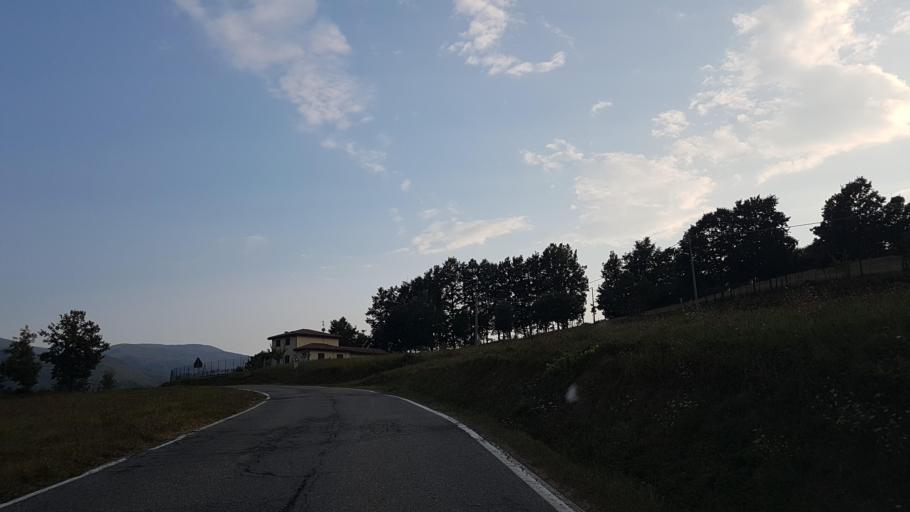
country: IT
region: Emilia-Romagna
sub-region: Provincia di Parma
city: Albareto
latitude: 44.4711
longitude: 9.7088
